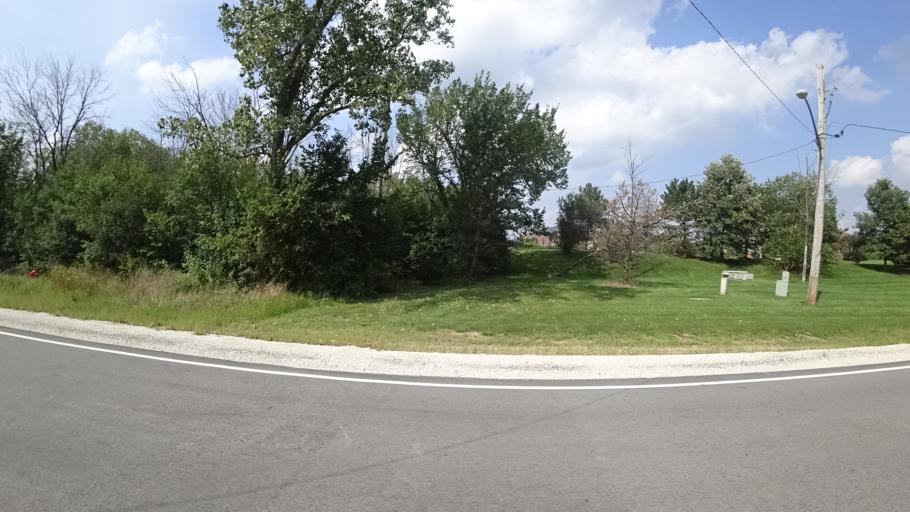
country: US
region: Illinois
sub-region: Will County
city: Goodings Grove
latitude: 41.6660
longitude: -87.8983
